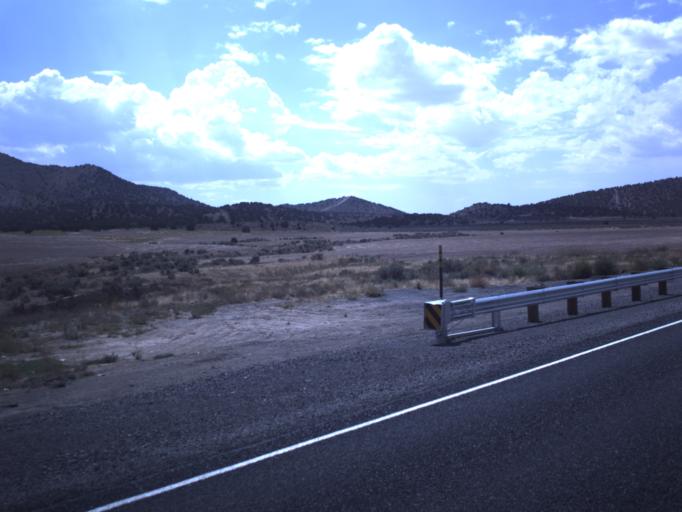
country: US
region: Utah
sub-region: Utah County
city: Eagle Mountain
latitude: 40.2392
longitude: -112.1546
